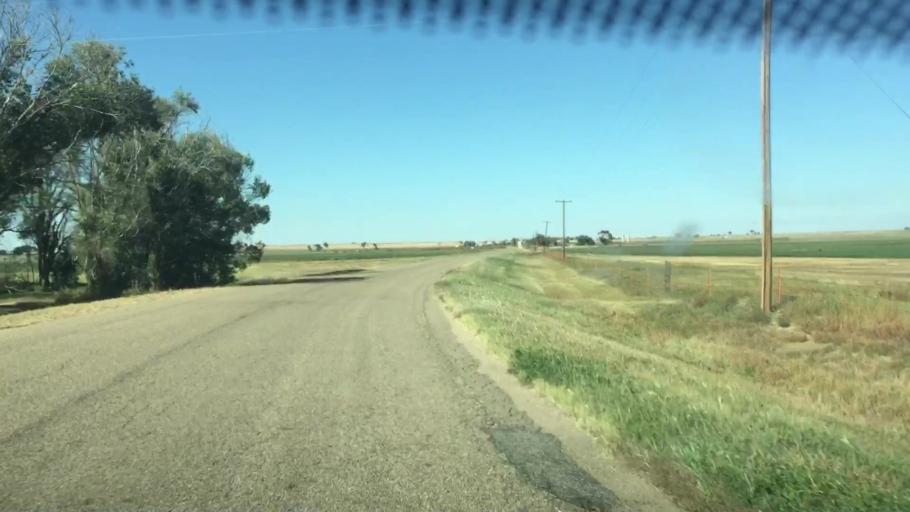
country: US
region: Colorado
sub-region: Prowers County
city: Lamar
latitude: 38.1010
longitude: -102.5214
